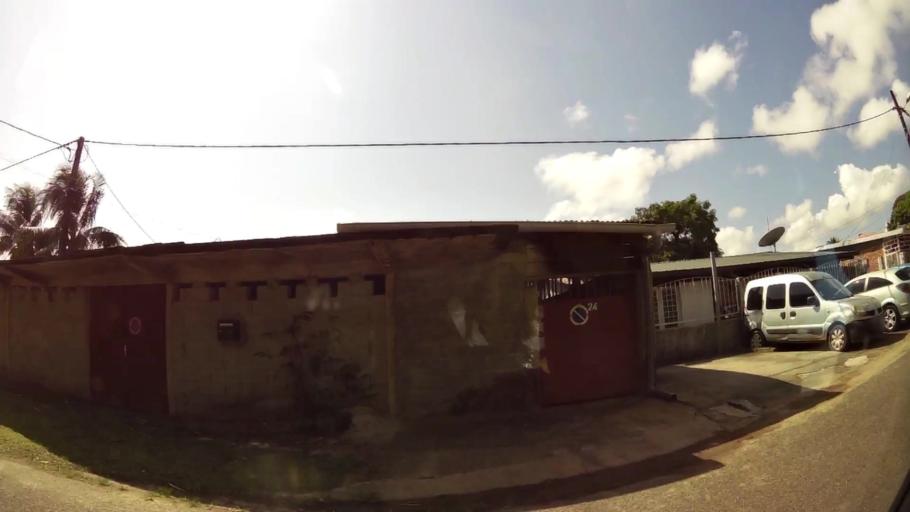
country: GF
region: Guyane
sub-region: Guyane
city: Cayenne
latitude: 4.9379
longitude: -52.3133
